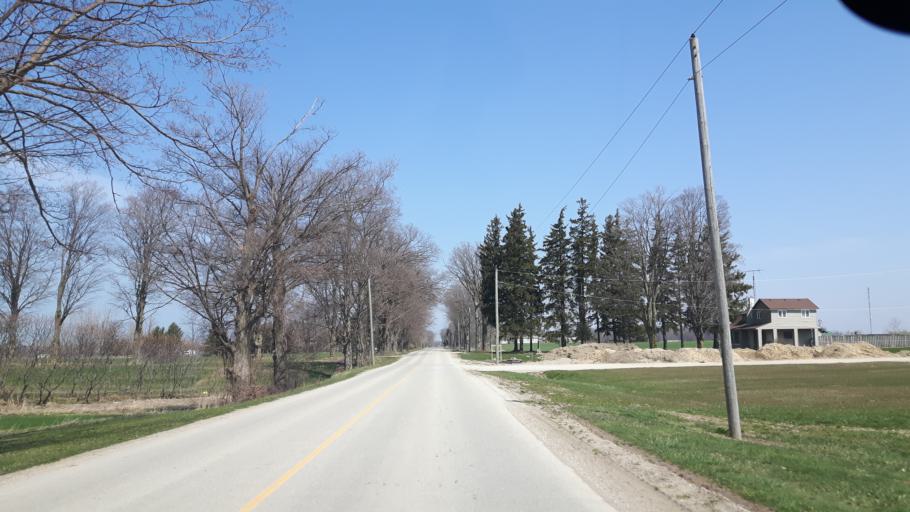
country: CA
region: Ontario
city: Goderich
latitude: 43.7030
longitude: -81.6849
